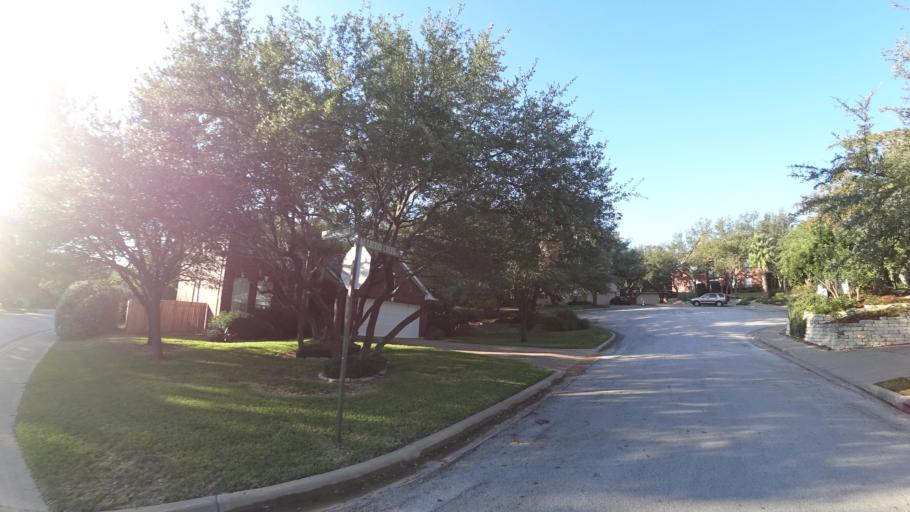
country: US
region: Texas
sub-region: Travis County
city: Hudson Bend
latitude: 30.3753
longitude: -97.8898
